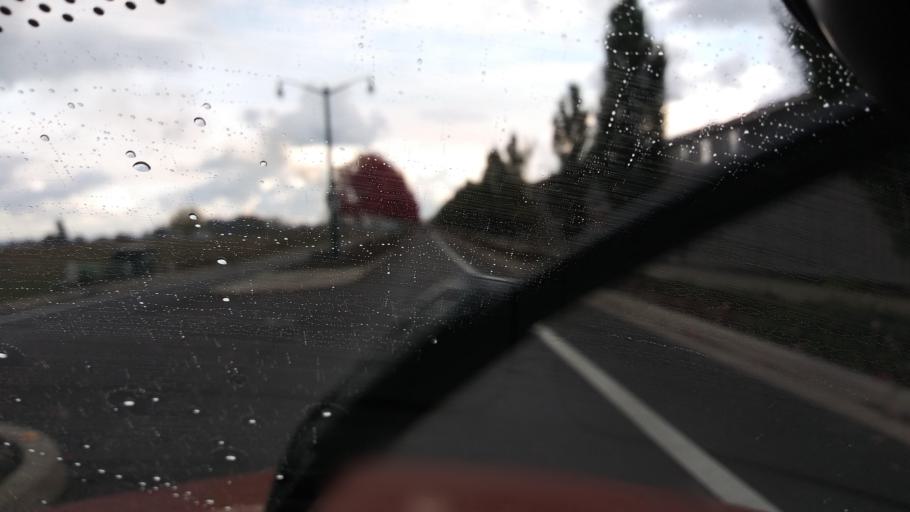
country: US
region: Oregon
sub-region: Washington County
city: Forest Grove
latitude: 45.5391
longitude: -123.1152
